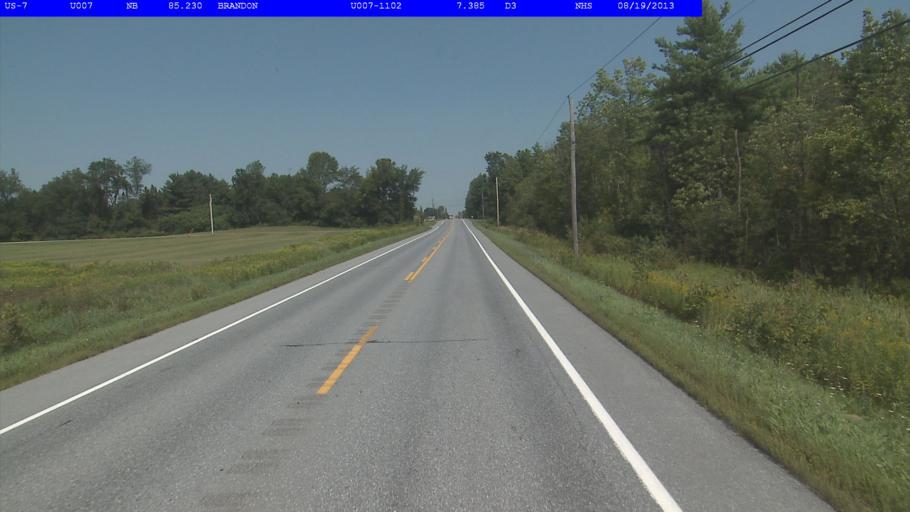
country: US
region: Vermont
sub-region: Rutland County
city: Brandon
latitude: 43.8427
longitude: -73.1061
